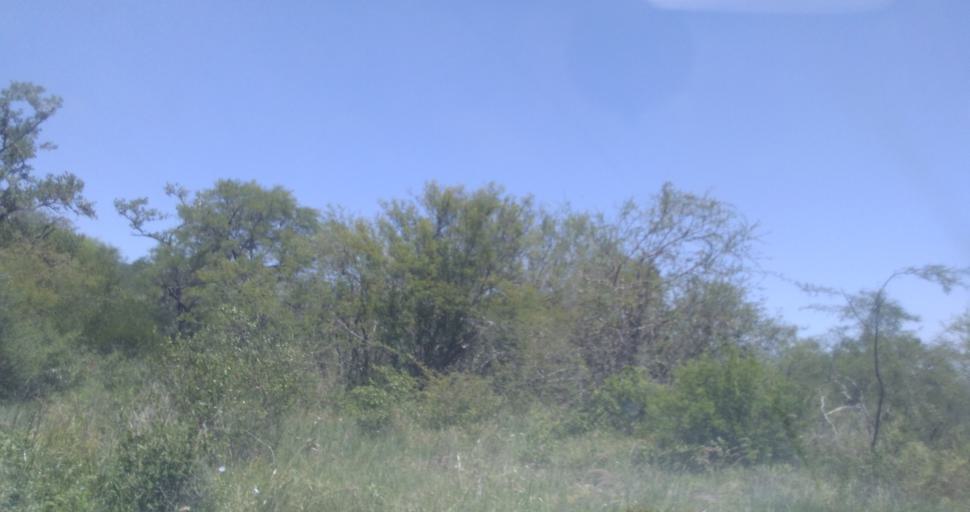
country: AR
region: Chaco
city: Fontana
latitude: -27.4760
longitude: -59.0733
